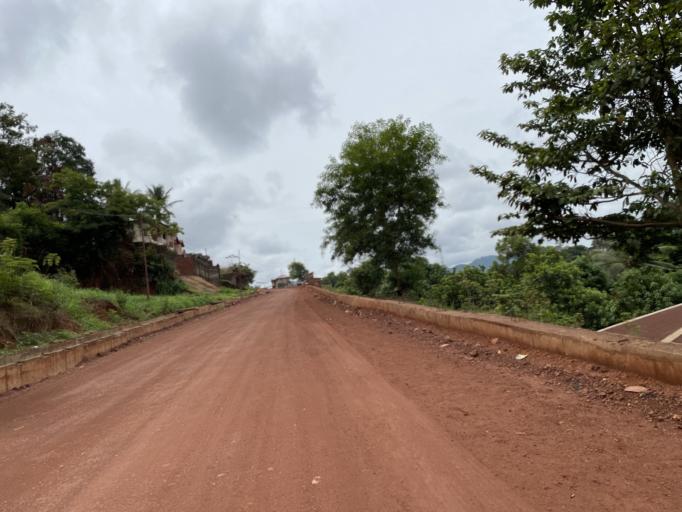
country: SL
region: Western Area
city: Hastings
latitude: 8.3990
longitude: -13.1506
